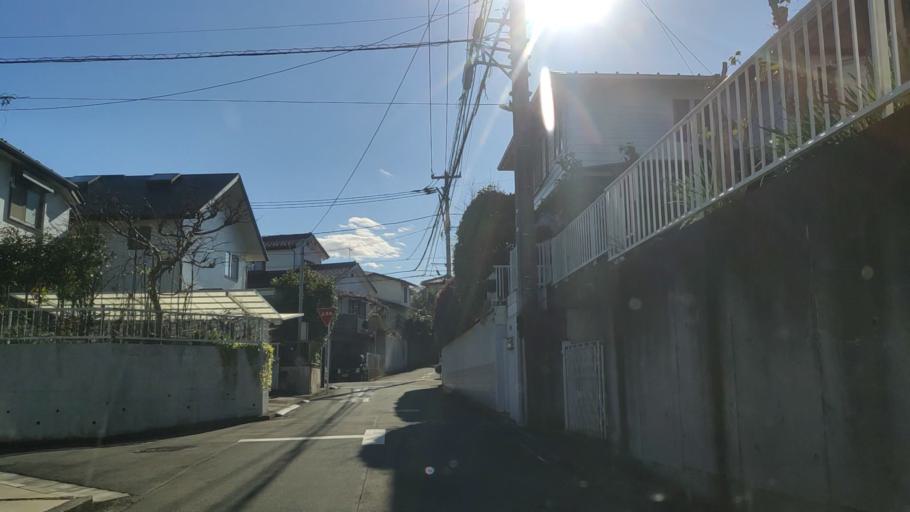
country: JP
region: Kanagawa
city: Minami-rinkan
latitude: 35.5072
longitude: 139.5252
